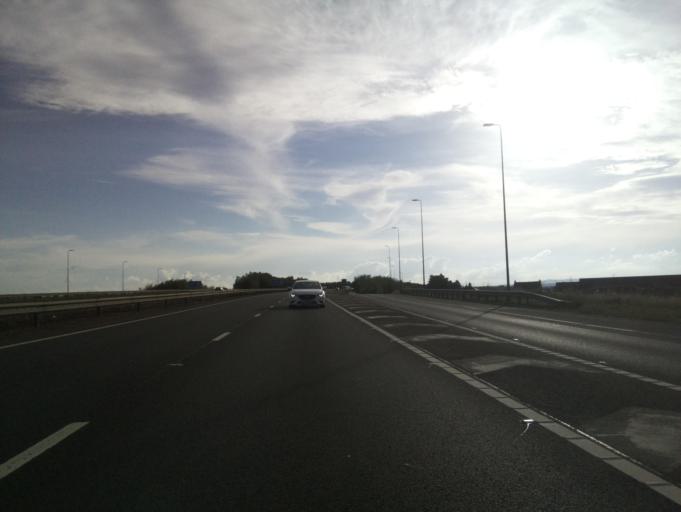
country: GB
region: Scotland
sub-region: Falkirk
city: Airth
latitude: 56.0546
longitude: -3.7549
